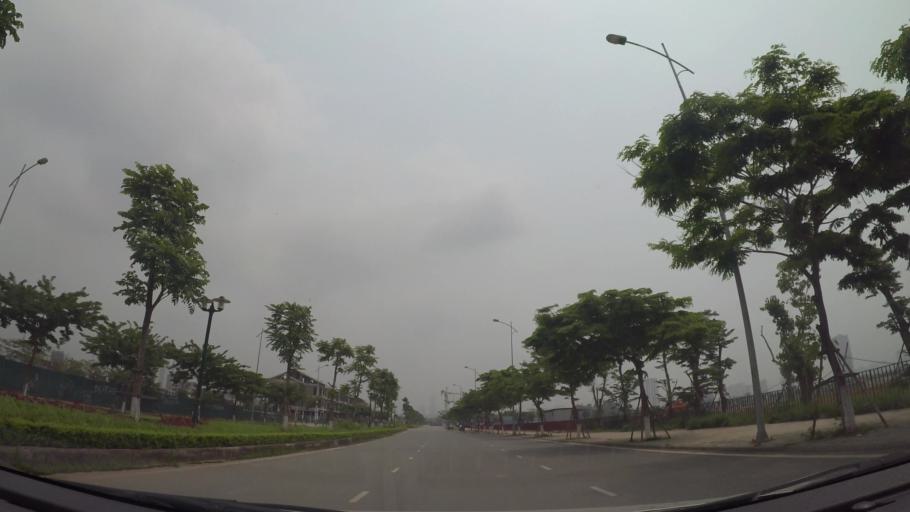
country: VN
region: Ha Noi
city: Ha Dong
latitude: 20.9814
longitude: 105.7552
